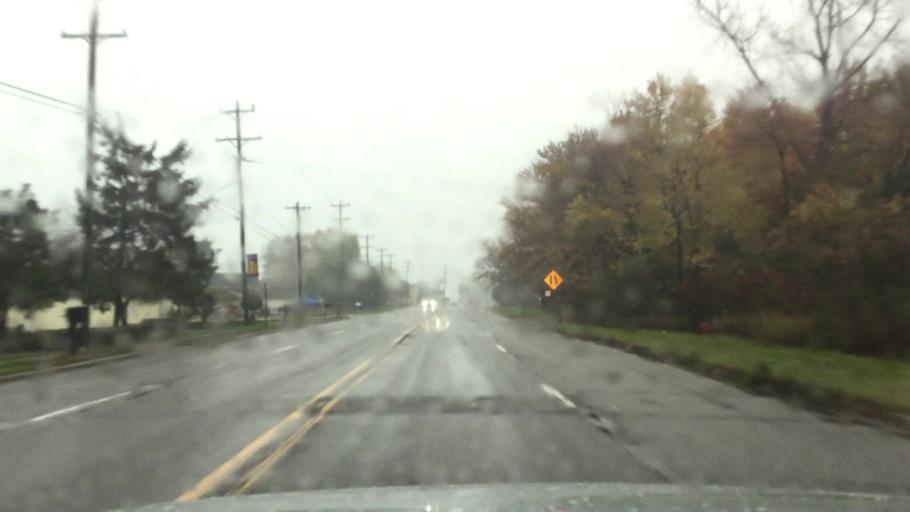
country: US
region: Michigan
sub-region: Macomb County
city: New Baltimore
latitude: 42.6817
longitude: -82.6623
